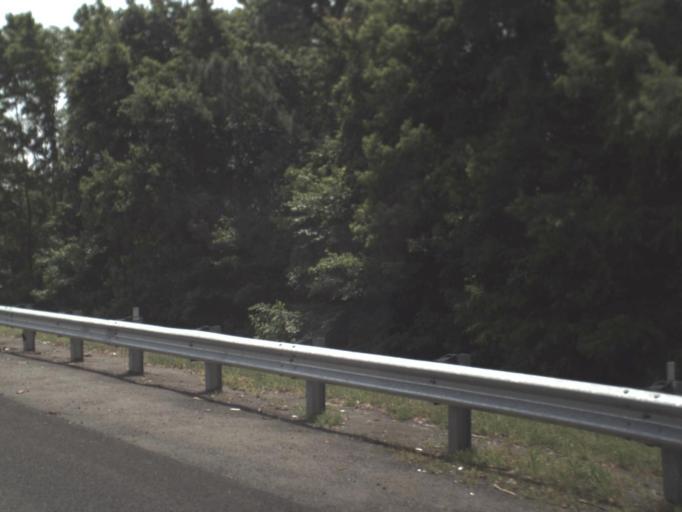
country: US
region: Florida
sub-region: Nassau County
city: Yulee
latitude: 30.6296
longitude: -81.5718
